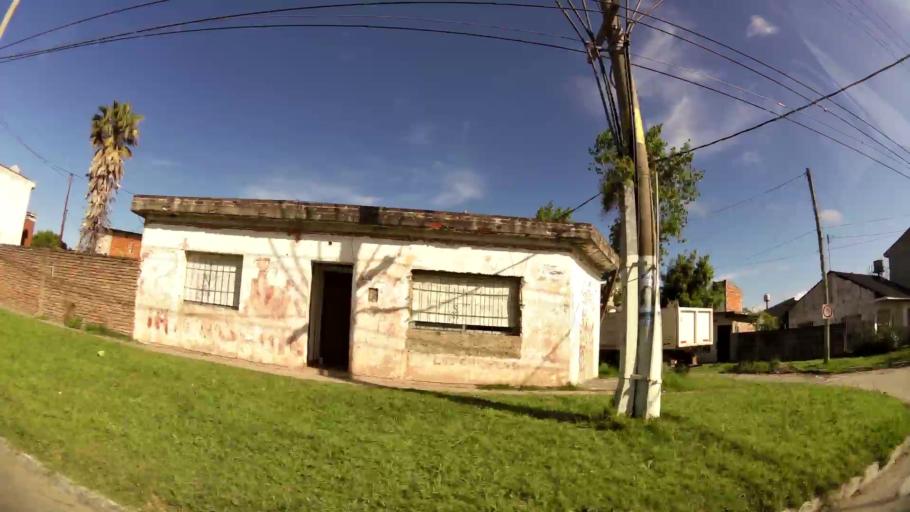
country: AR
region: Buenos Aires
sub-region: Partido de Quilmes
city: Quilmes
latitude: -34.7956
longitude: -58.2289
